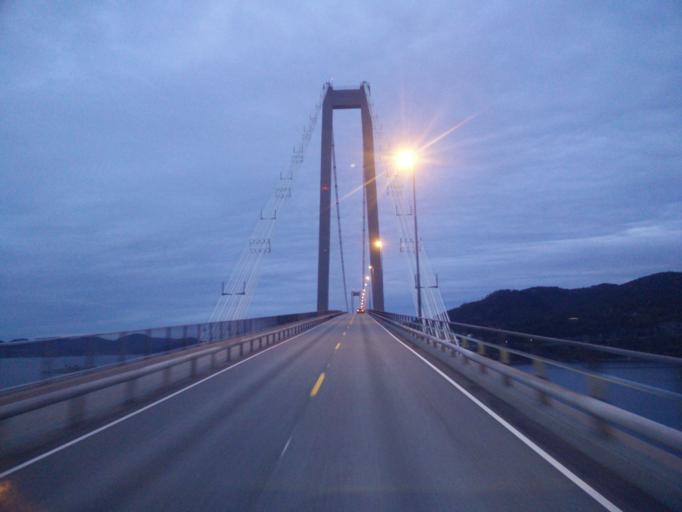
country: NO
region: More og Romsdal
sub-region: Gjemnes
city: Batnfjordsora
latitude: 62.9678
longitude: 7.7742
